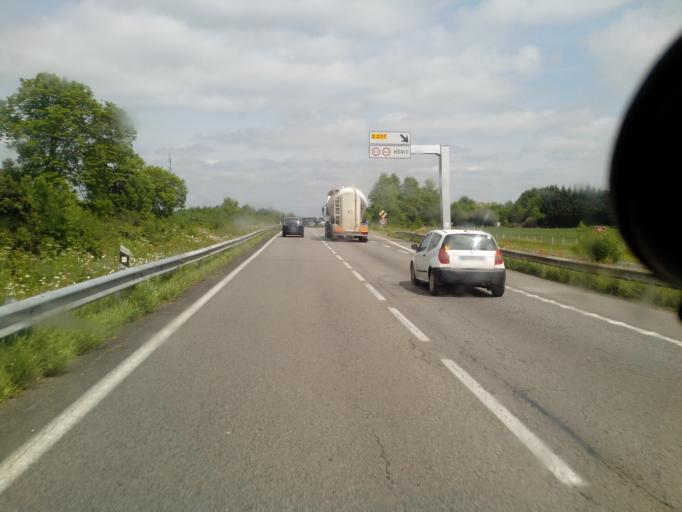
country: FR
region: Pays de la Loire
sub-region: Departement de la Loire-Atlantique
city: Heric
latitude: 47.3975
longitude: -1.6446
